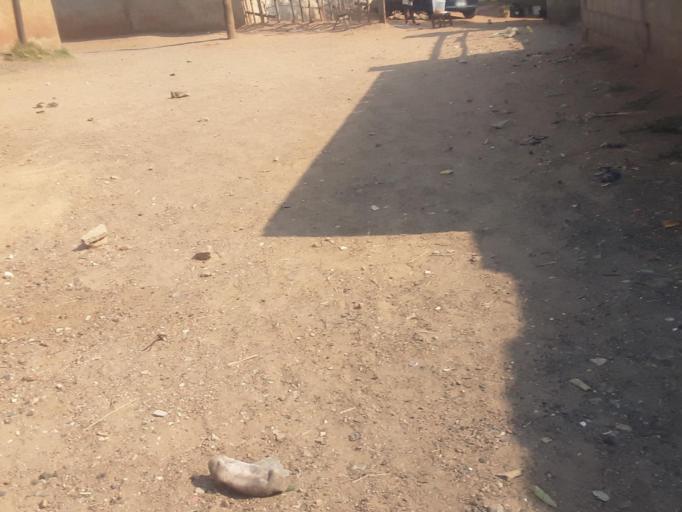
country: ZM
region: Lusaka
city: Lusaka
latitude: -15.3608
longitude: 28.3008
